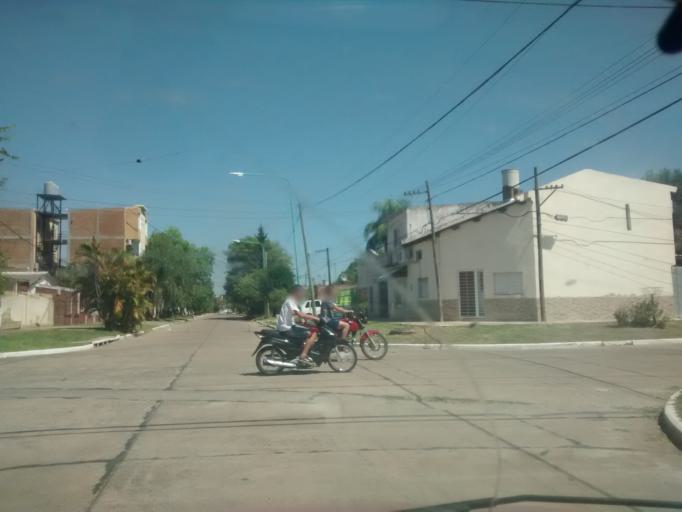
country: AR
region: Chaco
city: Resistencia
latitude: -27.4588
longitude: -59.0004
